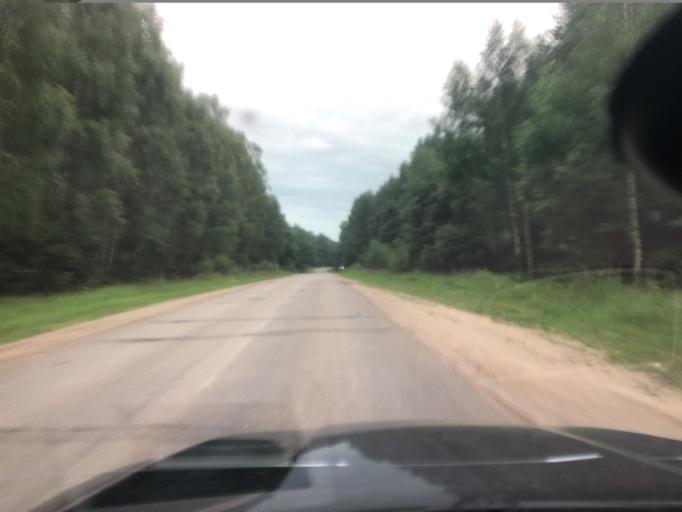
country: RU
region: Jaroslavl
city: Petrovsk
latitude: 56.9873
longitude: 39.1941
